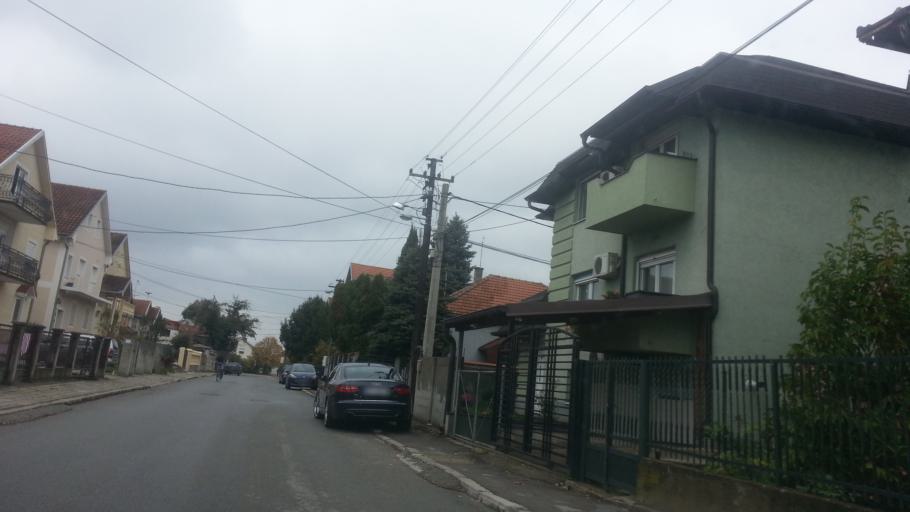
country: RS
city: Novi Banovci
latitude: 44.9077
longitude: 20.2857
